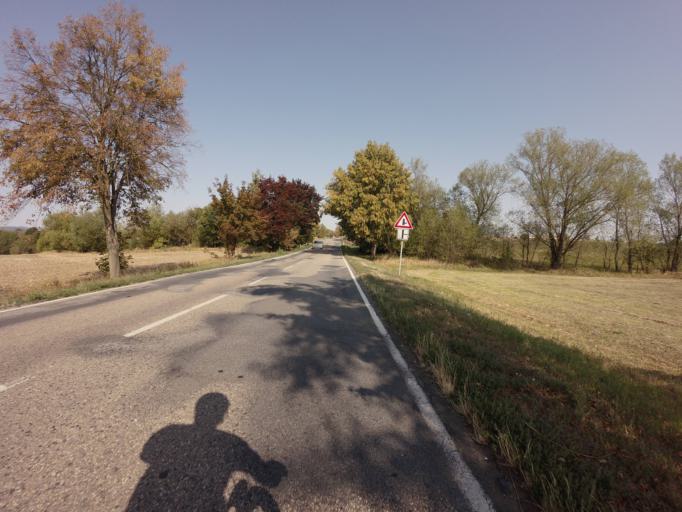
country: CZ
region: Central Bohemia
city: Porici nad Sazavou
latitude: 49.8119
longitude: 14.6449
